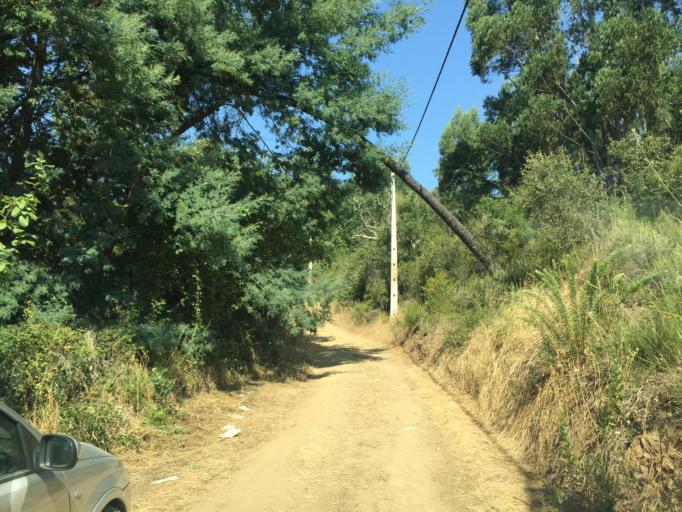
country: PT
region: Santarem
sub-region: Ferreira do Zezere
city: Ferreira do Zezere
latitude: 39.6048
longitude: -8.2780
